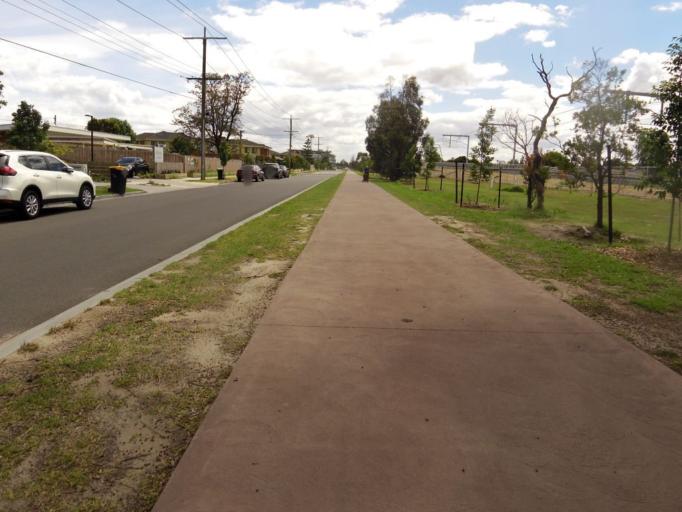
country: AU
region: Victoria
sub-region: Kingston
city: Clayton South
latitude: -37.9332
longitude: 145.1314
